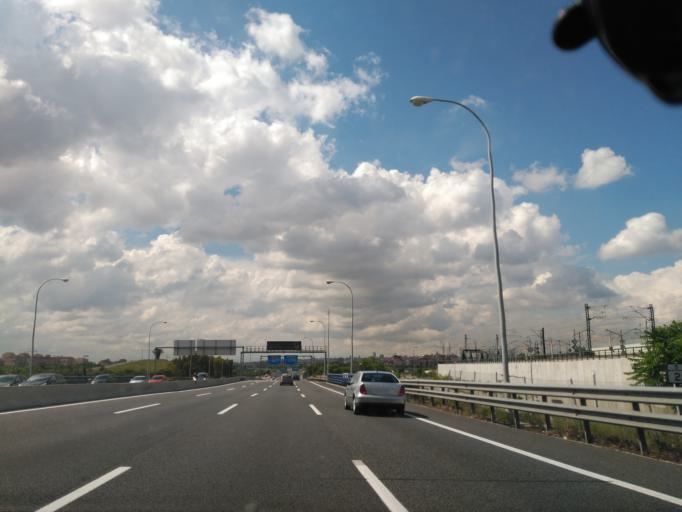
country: ES
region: Madrid
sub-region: Provincia de Madrid
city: Usera
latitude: 40.3738
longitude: -3.6814
